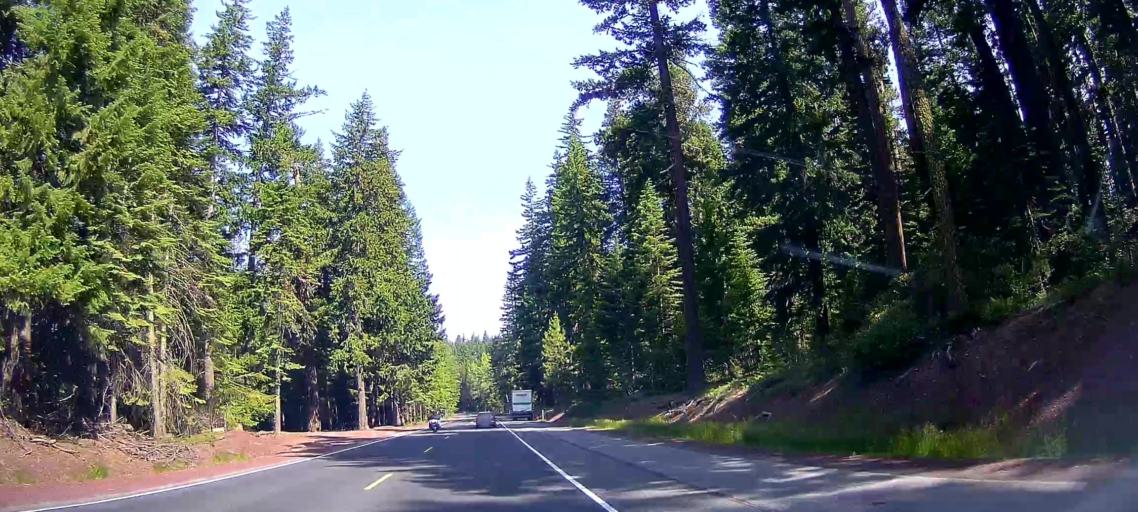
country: US
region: Oregon
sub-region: Clackamas County
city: Mount Hood Village
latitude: 45.1232
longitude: -121.5857
